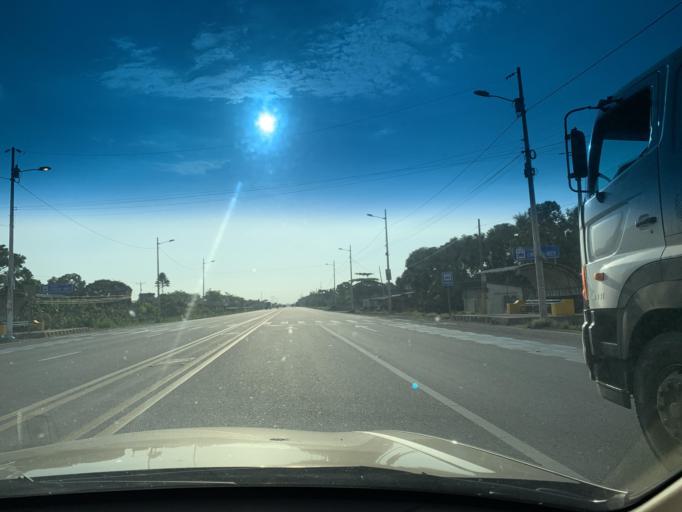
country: EC
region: Guayas
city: Naranjito
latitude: -2.2561
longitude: -79.5964
